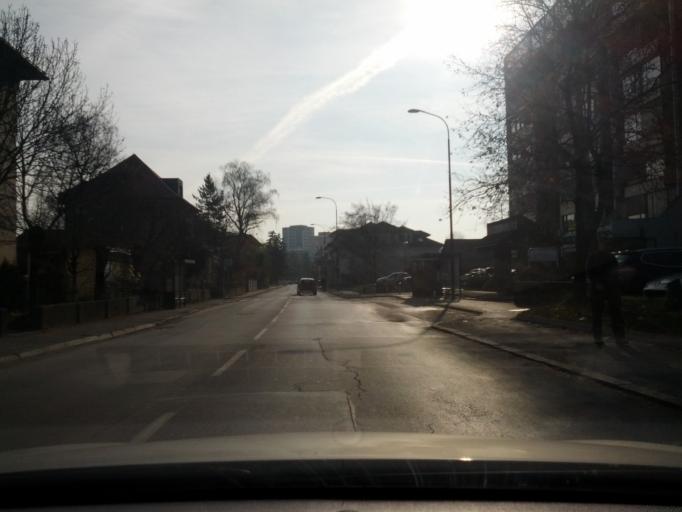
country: SI
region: Ljubljana
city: Ljubljana
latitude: 46.0657
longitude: 14.5029
